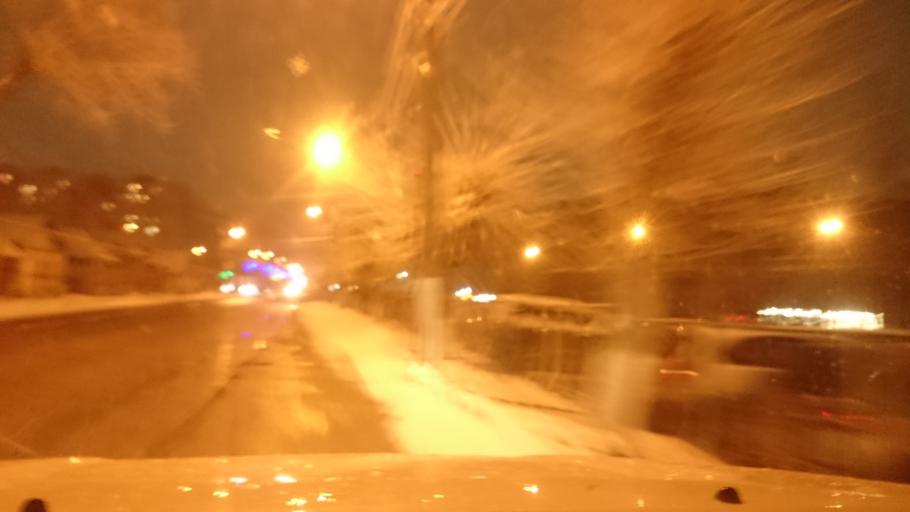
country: RU
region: Tula
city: Tula
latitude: 54.2159
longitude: 37.6050
